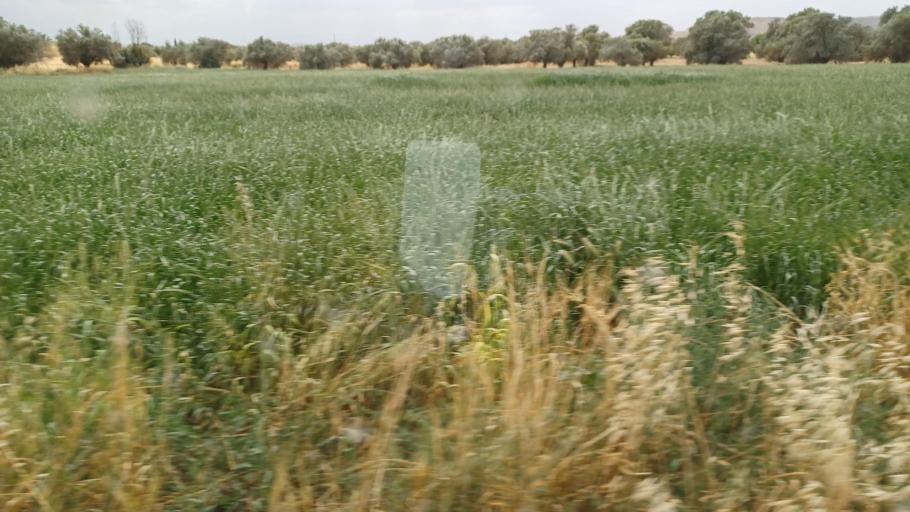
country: CY
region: Larnaka
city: Athienou
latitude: 35.0734
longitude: 33.5394
